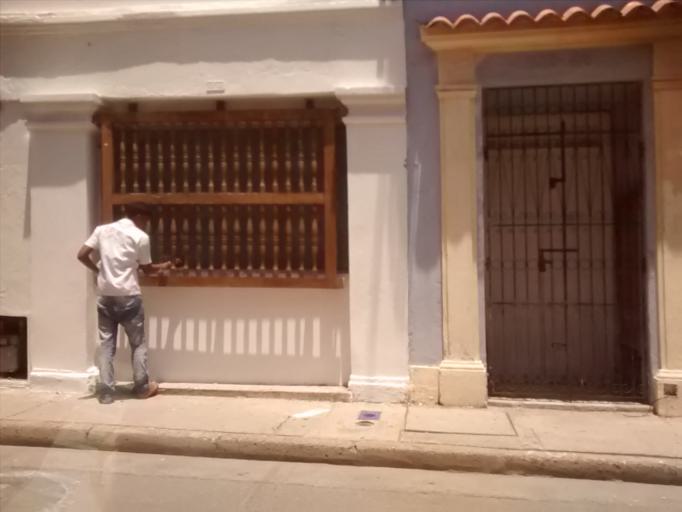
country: CO
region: Bolivar
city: Cartagena
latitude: 10.4184
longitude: -75.5459
